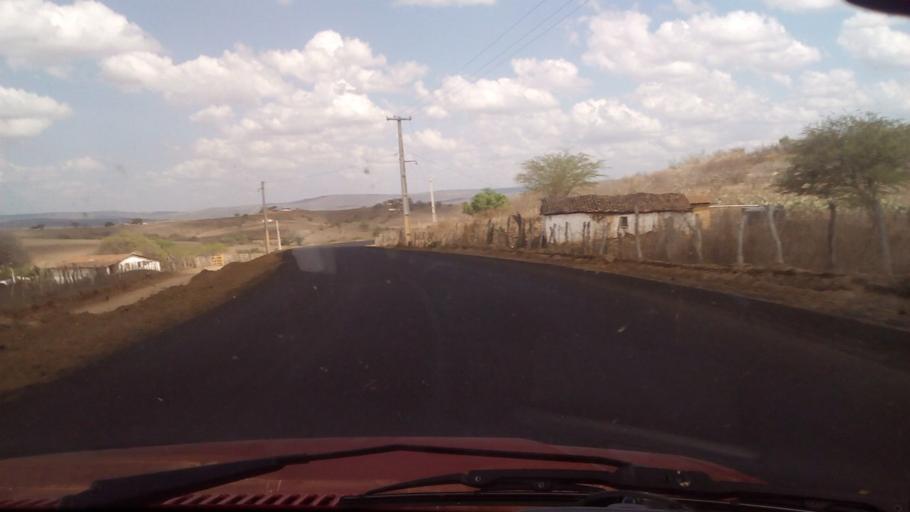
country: BR
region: Paraiba
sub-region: Cacimba De Dentro
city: Cacimba de Dentro
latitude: -6.6586
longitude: -35.7636
